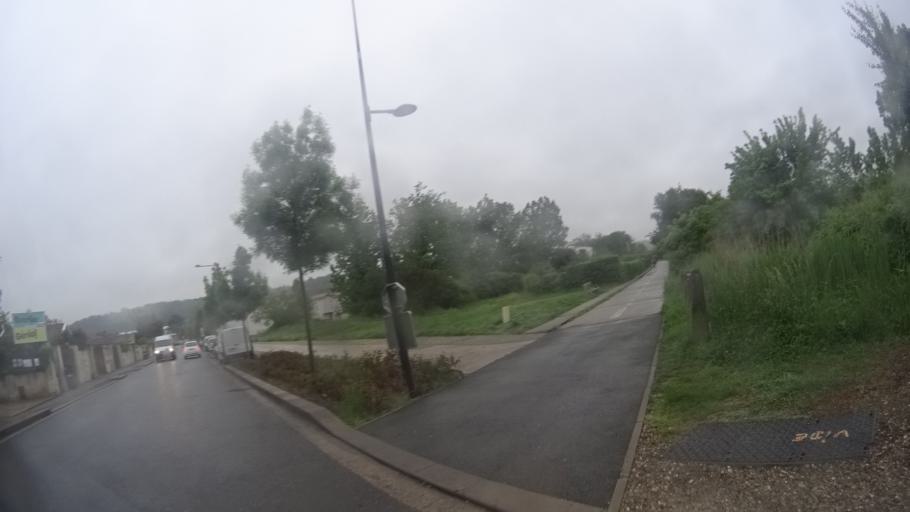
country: FR
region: Aquitaine
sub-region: Departement de la Gironde
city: Floirac
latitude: 44.8361
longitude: -0.5386
